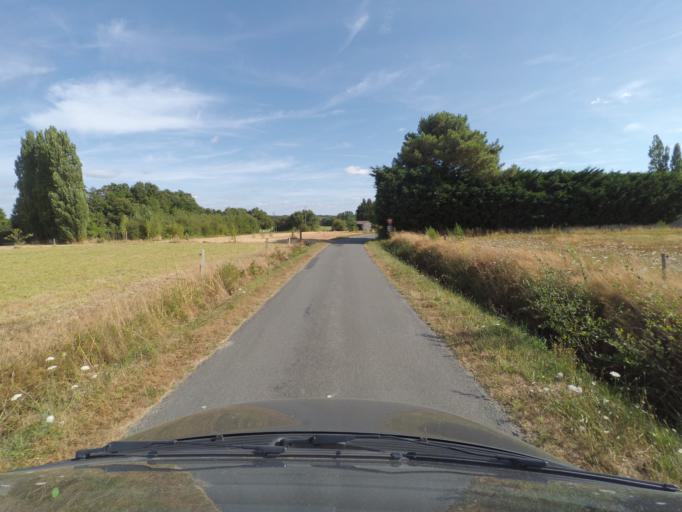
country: FR
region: Pays de la Loire
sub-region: Departement de la Loire-Atlantique
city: Le Bignon
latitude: 47.0878
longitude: -1.4609
